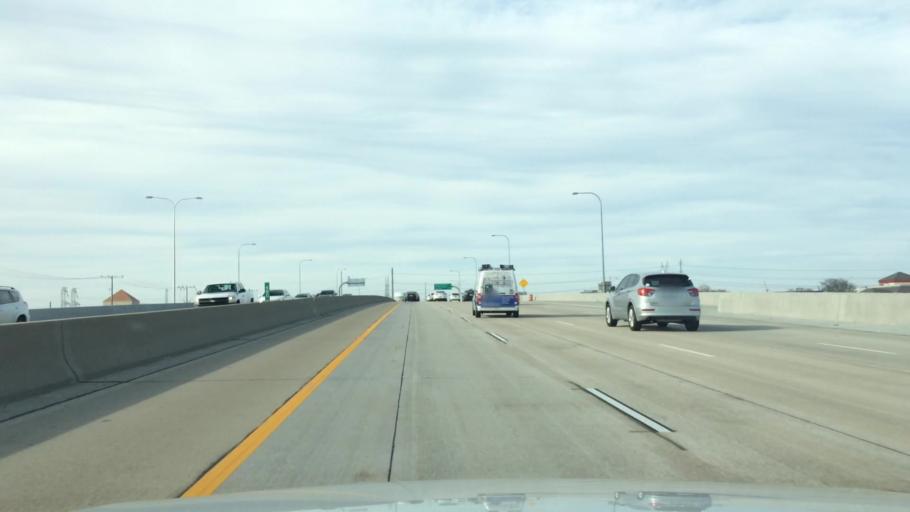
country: US
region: Texas
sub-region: Denton County
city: The Colony
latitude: 33.0525
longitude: -96.8298
